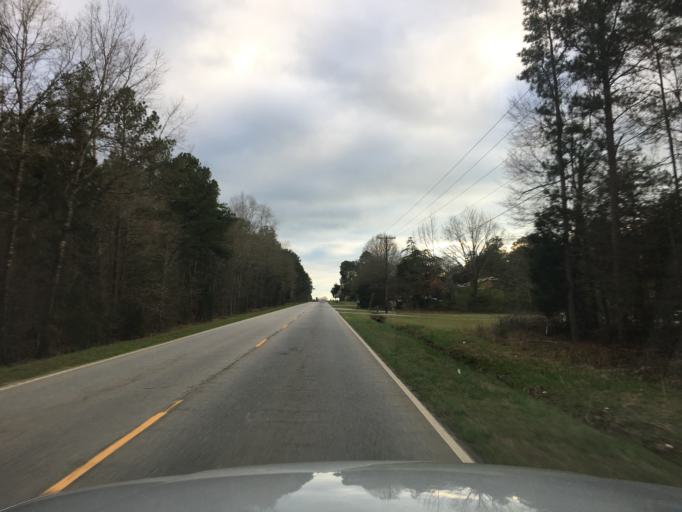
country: US
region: South Carolina
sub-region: Saluda County
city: Saluda
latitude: 33.9743
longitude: -81.7761
